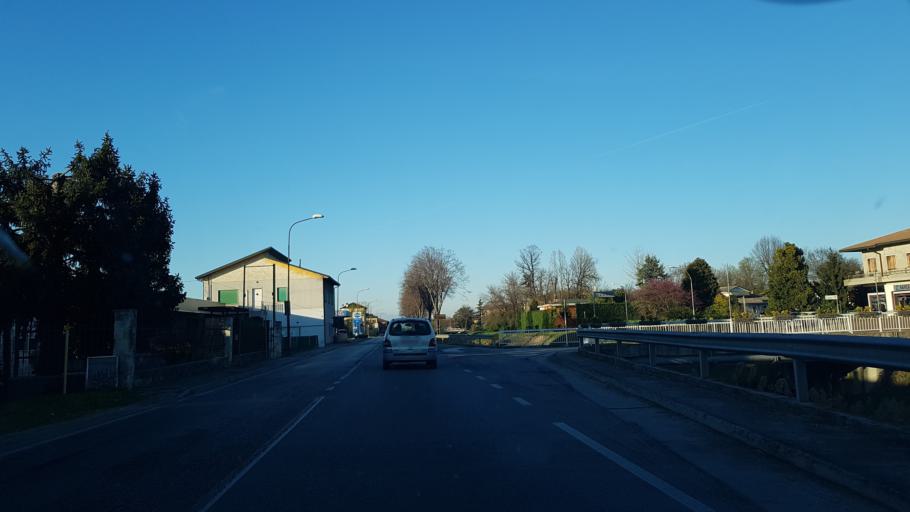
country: IT
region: Veneto
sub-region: Provincia di Vicenza
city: Ponte di Barbarano
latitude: 45.3894
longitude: 11.5741
